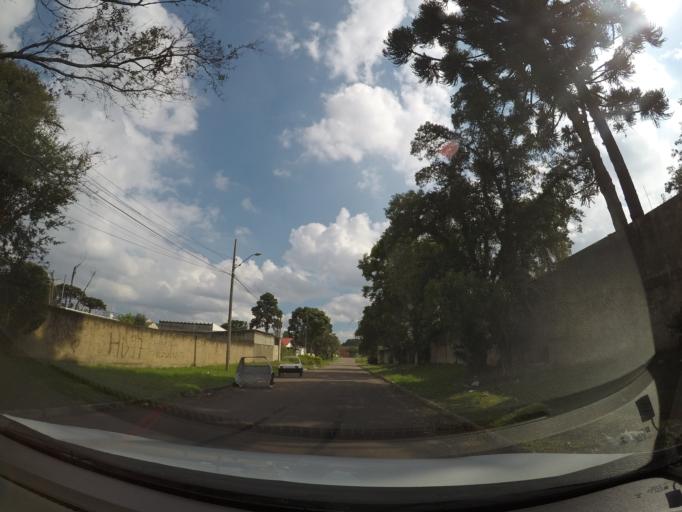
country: BR
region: Parana
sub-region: Curitiba
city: Curitiba
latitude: -25.4857
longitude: -49.2624
